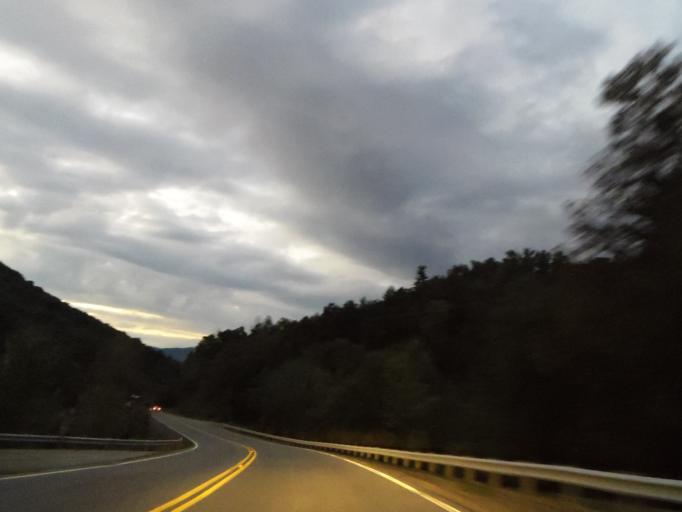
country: US
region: North Carolina
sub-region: Madison County
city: Marshall
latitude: 35.8906
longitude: -82.7481
